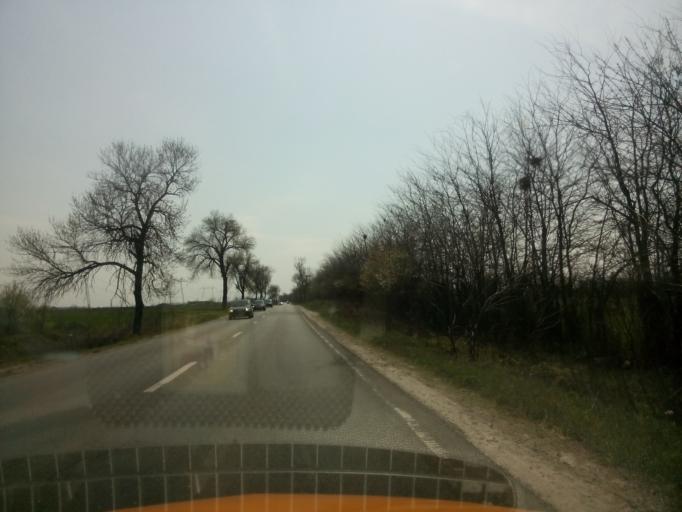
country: RO
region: Ilfov
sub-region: Comuna Glina
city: Glina
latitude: 44.3225
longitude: 26.2660
